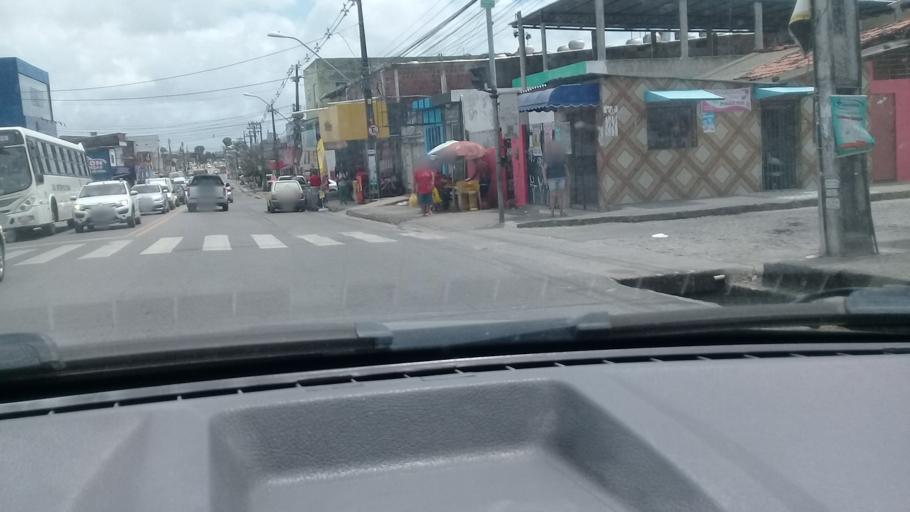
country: BR
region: Pernambuco
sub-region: Jaboatao Dos Guararapes
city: Jaboatao dos Guararapes
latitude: -8.1168
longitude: -34.9413
